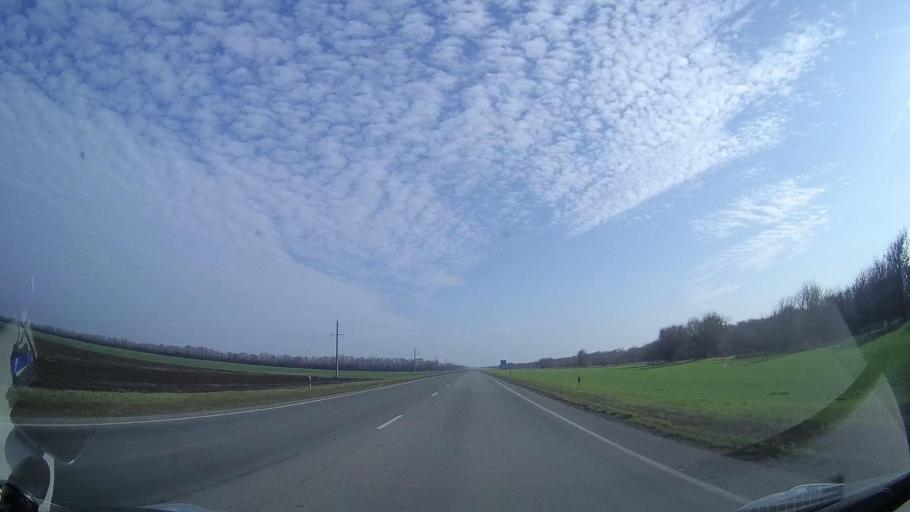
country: RU
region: Rostov
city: Gigant
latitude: 46.5236
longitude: 41.2671
